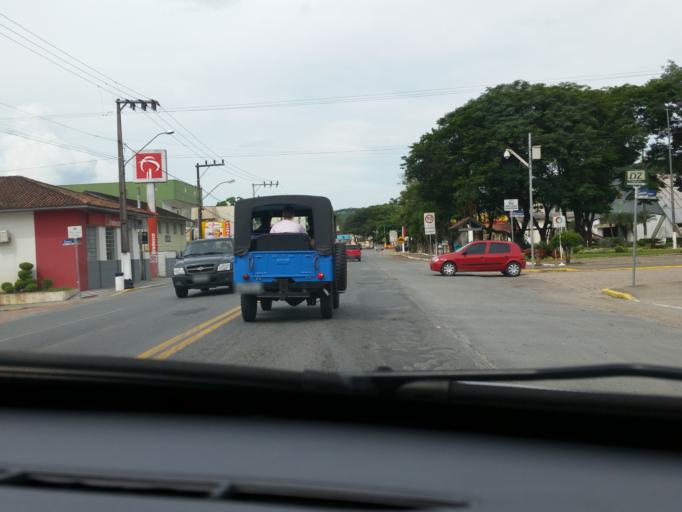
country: BR
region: Santa Catarina
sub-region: Rodeio
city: Gavea
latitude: -27.0331
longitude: -49.3864
